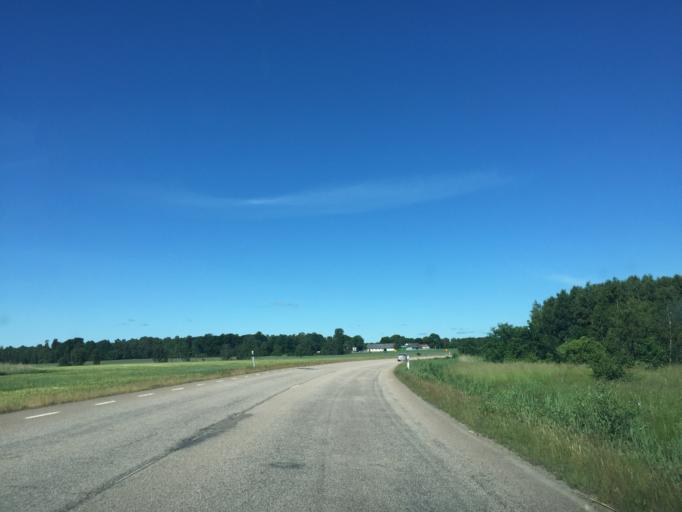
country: SE
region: Skane
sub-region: Angelholms Kommun
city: AEngelholm
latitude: 56.2231
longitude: 12.8472
